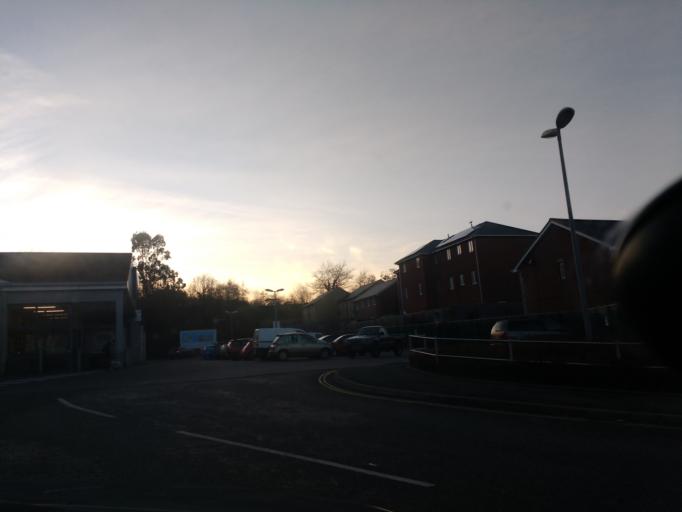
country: GB
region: England
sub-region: Isle of Wight
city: Shanklin
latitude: 50.6339
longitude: -1.1815
